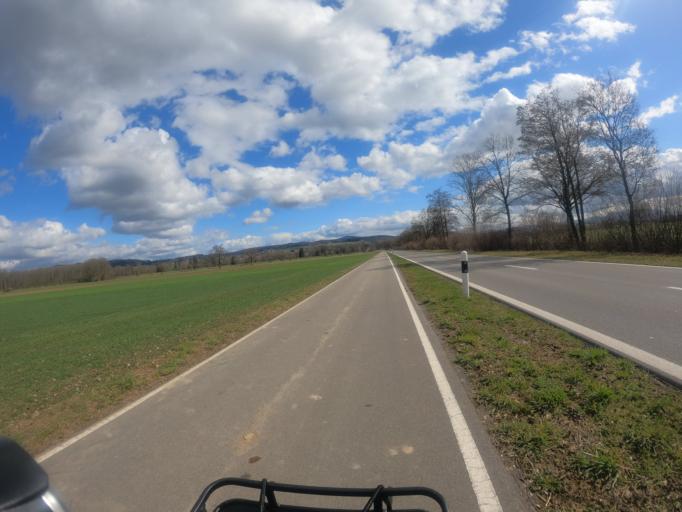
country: CH
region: Aargau
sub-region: Bezirk Bremgarten
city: Jonen
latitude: 47.2803
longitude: 8.3834
